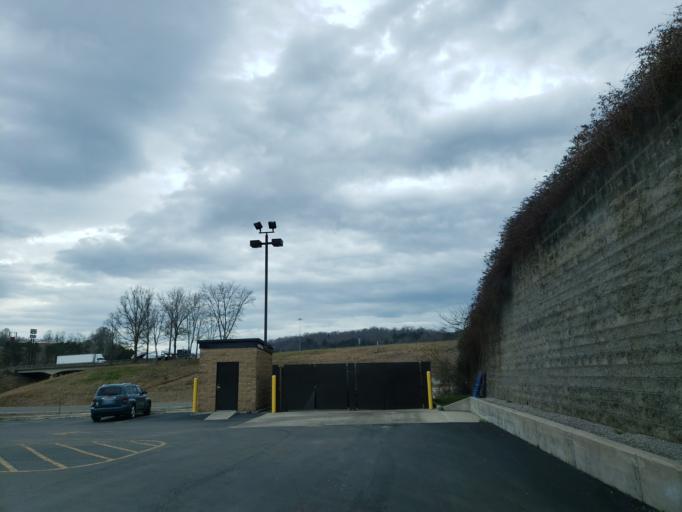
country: US
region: Kentucky
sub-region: Whitley County
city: Corbin
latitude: 36.9192
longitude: -84.1277
